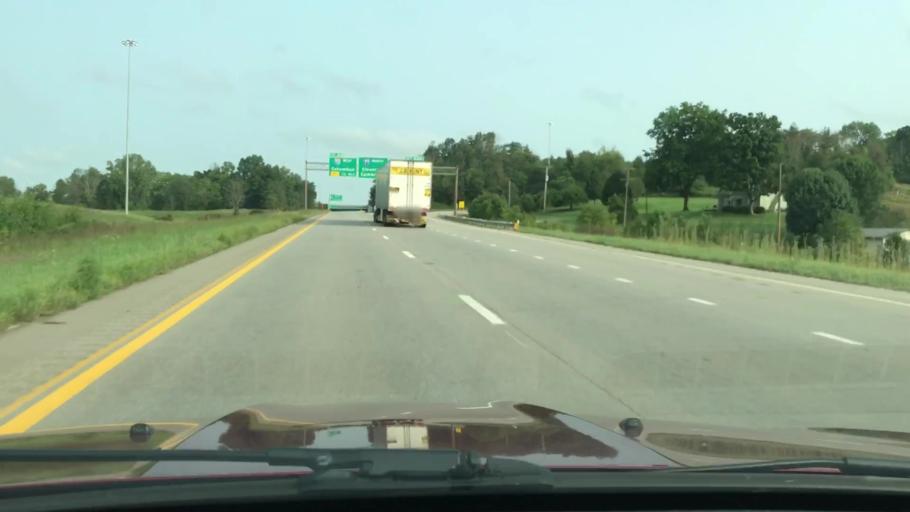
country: US
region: Ohio
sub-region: Guernsey County
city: Byesville
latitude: 39.9944
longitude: -81.5516
